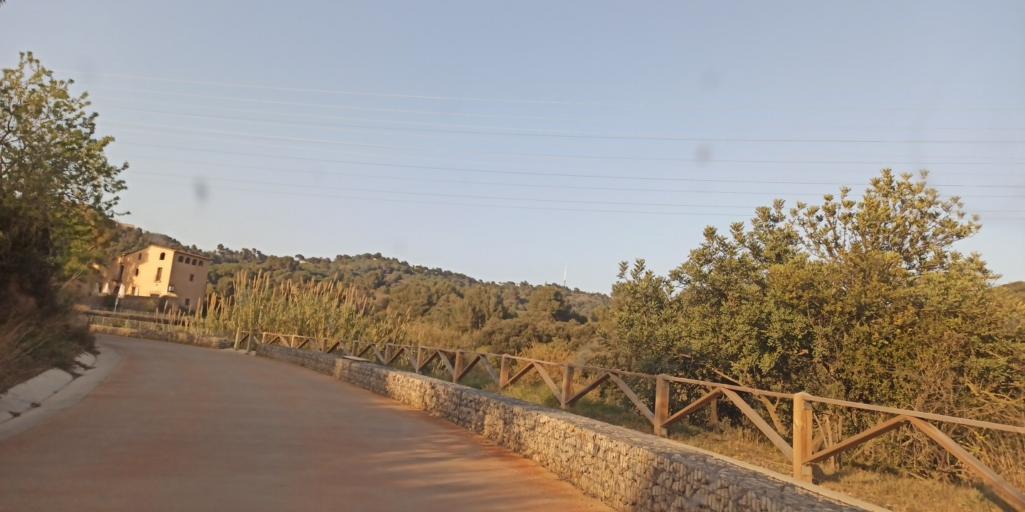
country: ES
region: Catalonia
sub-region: Provincia de Barcelona
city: Sant Just Desvern
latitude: 41.3985
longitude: 2.0856
